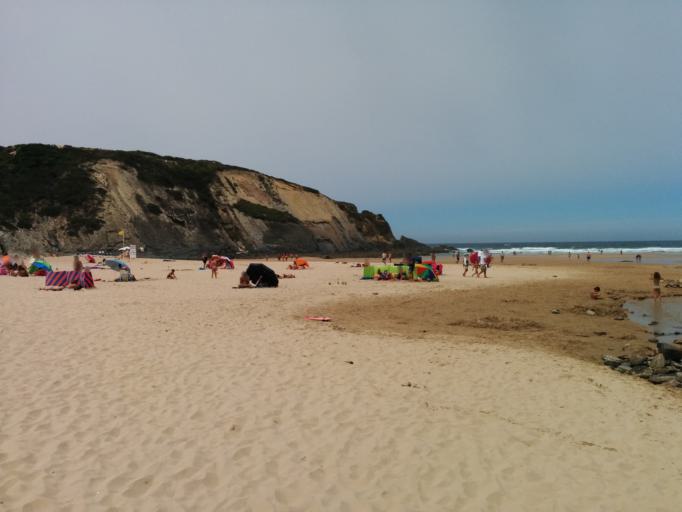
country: PT
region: Beja
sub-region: Odemira
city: Sao Teotonio
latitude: 37.5001
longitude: -8.7912
